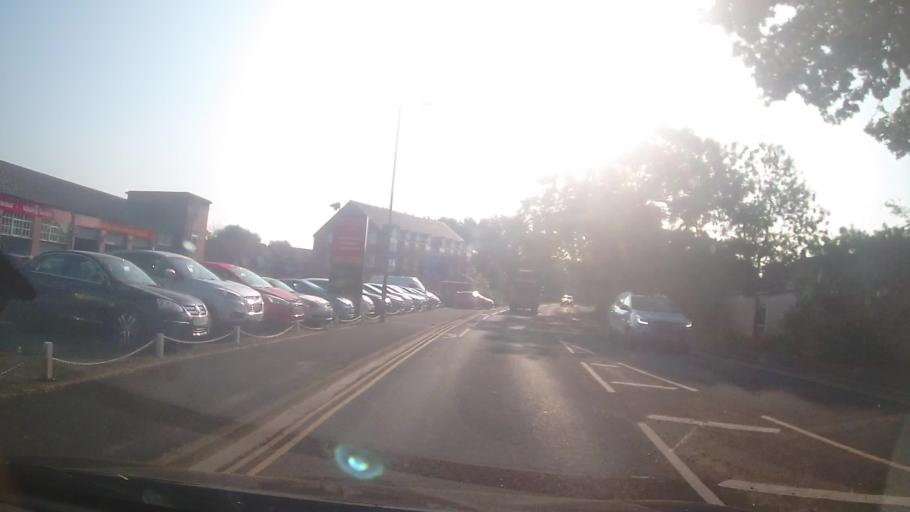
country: GB
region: England
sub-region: Shropshire
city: Astley
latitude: 52.7346
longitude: -2.7178
